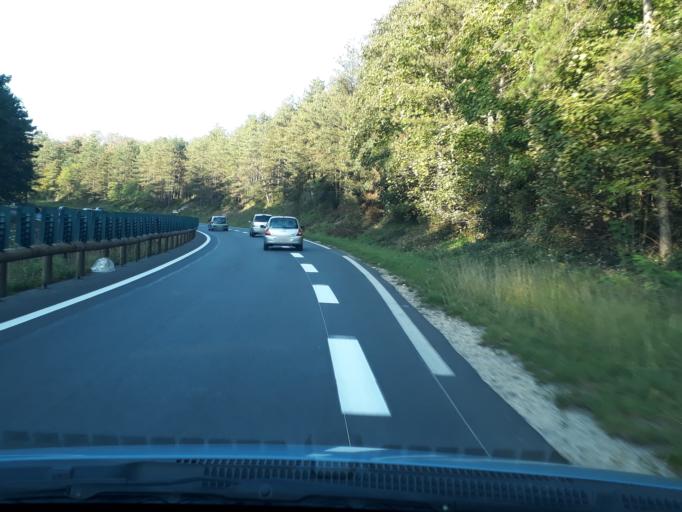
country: FR
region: Ile-de-France
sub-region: Departement de Seine-et-Marne
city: Avon
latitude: 48.4221
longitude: 2.7102
